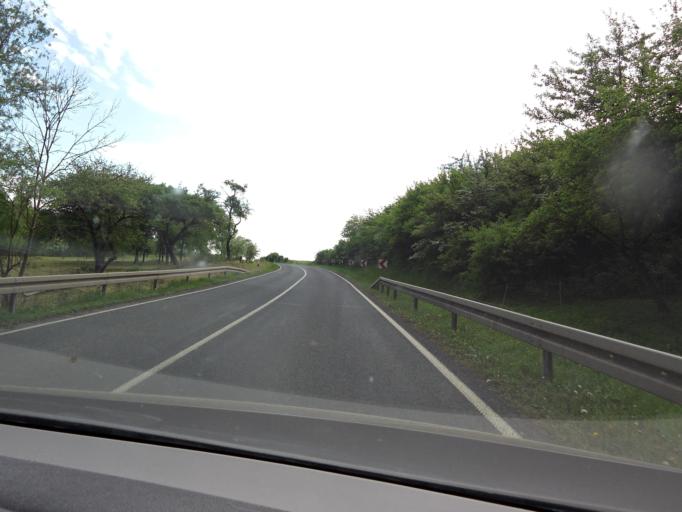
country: DE
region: Thuringia
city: Klettstedt
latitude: 51.1431
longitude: 10.7519
